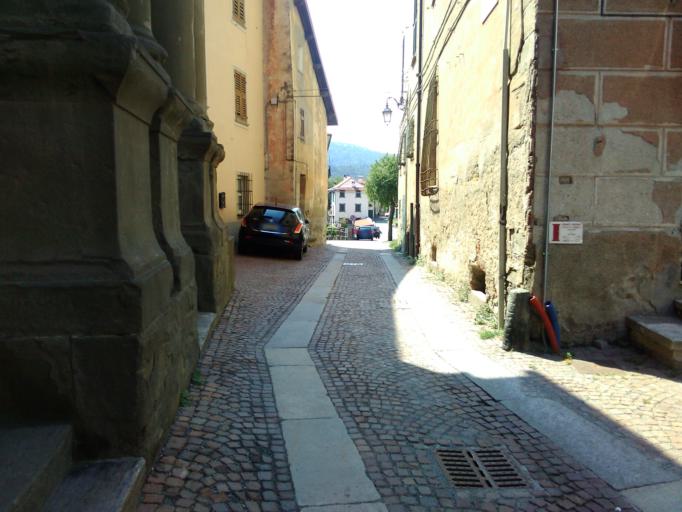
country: IT
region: Liguria
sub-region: Provincia di Savona
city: Sassello
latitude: 44.4782
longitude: 8.4897
